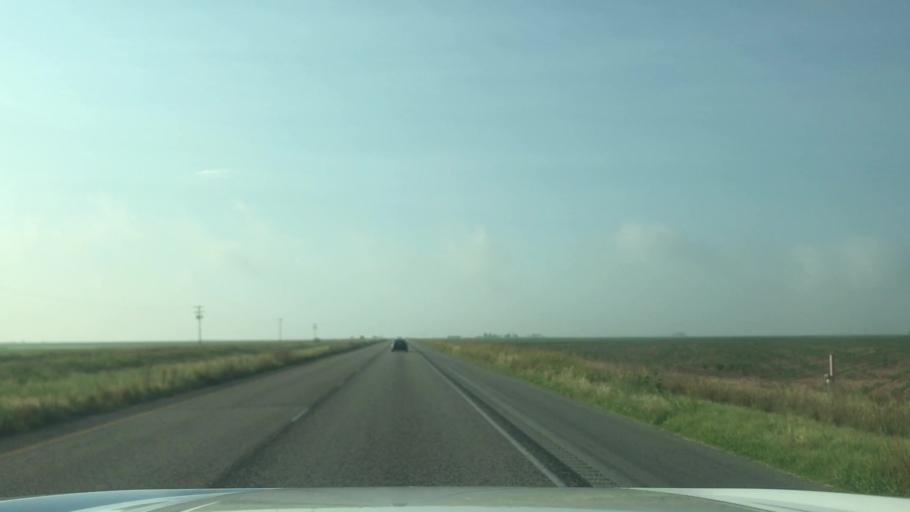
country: US
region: Texas
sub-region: Lubbock County
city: Slaton
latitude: 33.3273
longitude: -101.5313
